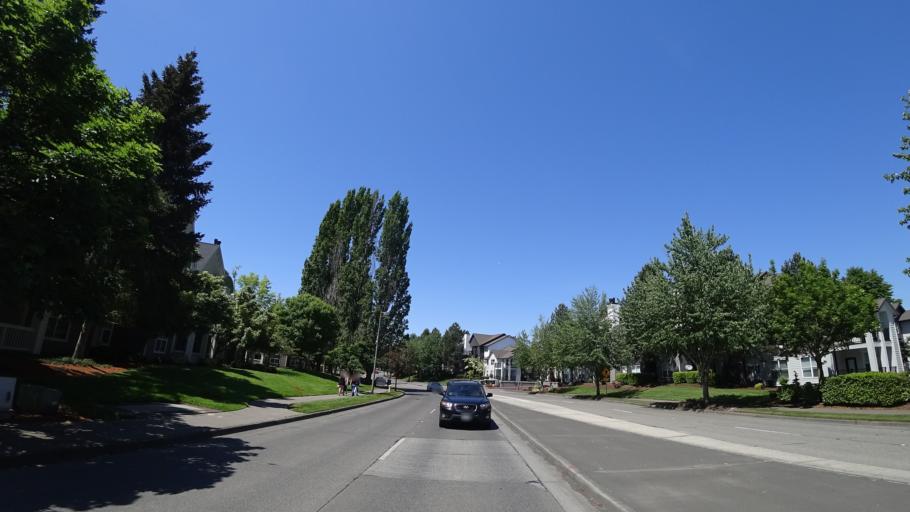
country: US
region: Oregon
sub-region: Washington County
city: Beaverton
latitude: 45.4956
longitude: -122.8310
